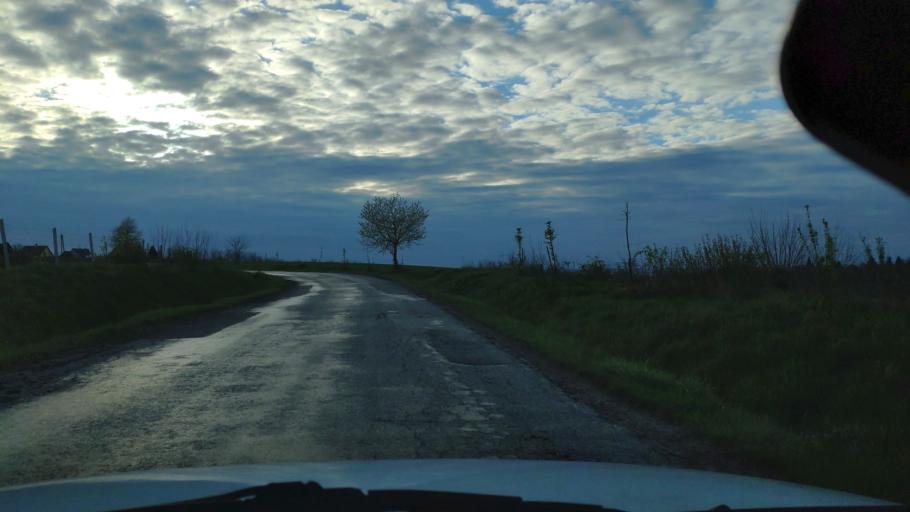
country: HU
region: Zala
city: Nagykanizsa
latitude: 46.4302
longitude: 17.0510
